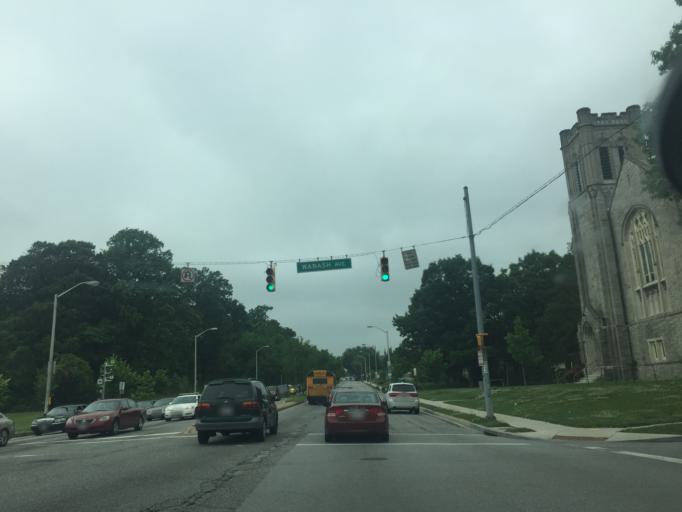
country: US
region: Maryland
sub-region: Baltimore County
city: Lochearn
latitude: 39.3227
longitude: -76.6664
